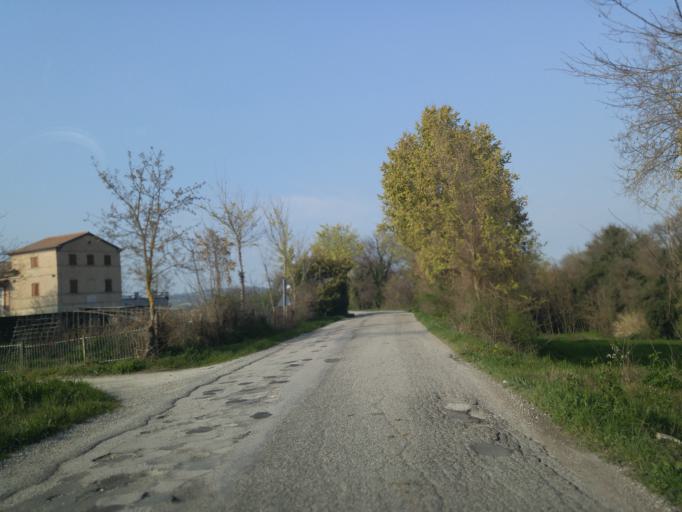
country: IT
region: The Marches
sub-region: Provincia di Pesaro e Urbino
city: Tavernelle
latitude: 43.7071
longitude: 12.8875
